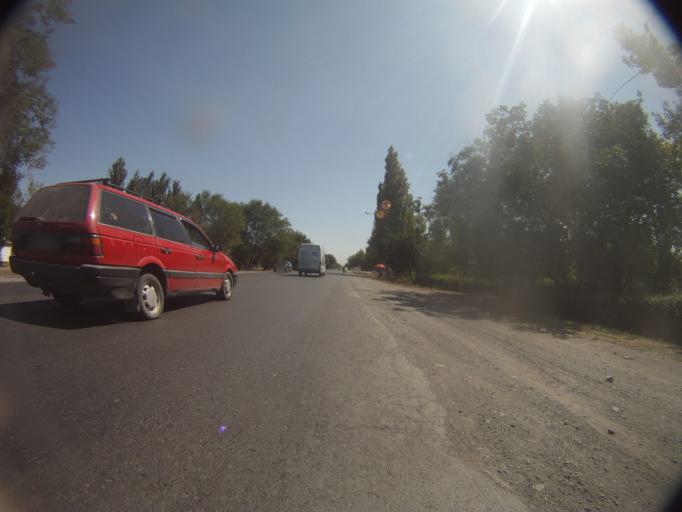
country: KG
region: Chuy
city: Belovodskoye
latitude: 42.8413
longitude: 74.0369
